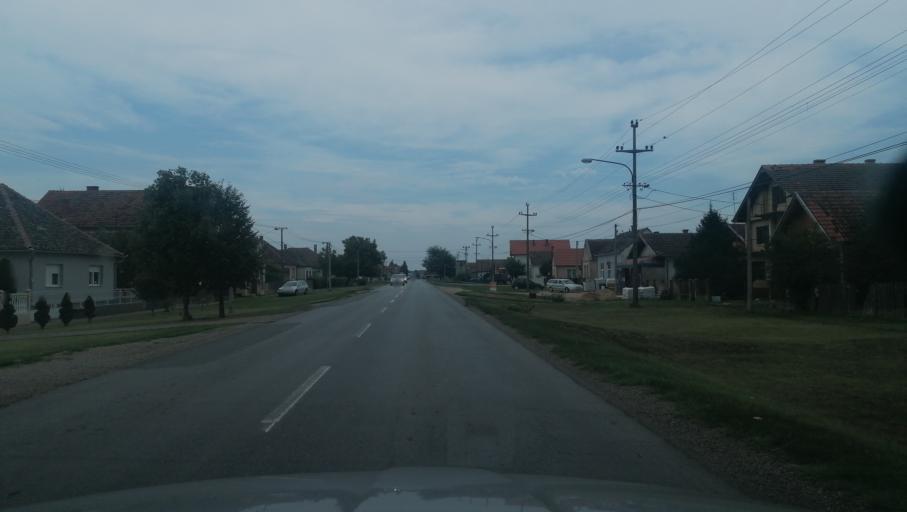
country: RS
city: Salas Nocajski
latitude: 44.9458
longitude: 19.5837
